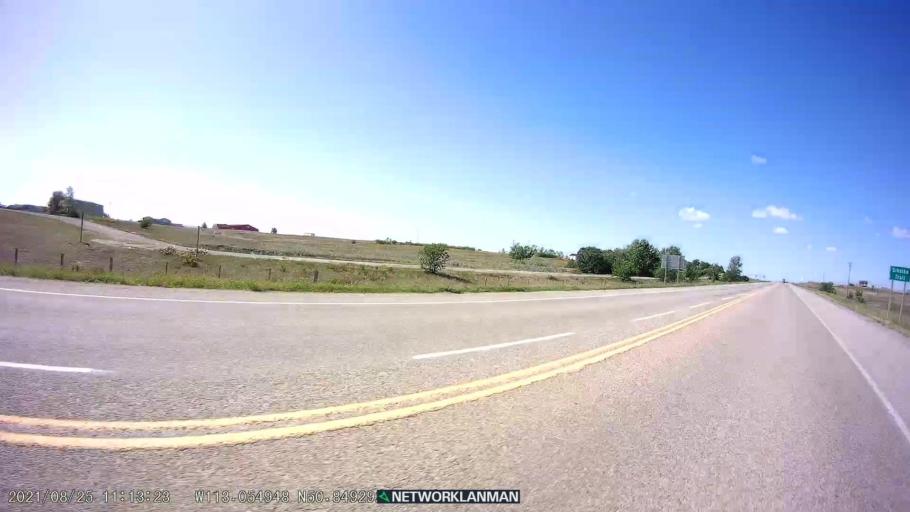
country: CA
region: Alberta
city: Strathmore
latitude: 50.8500
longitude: -113.0531
